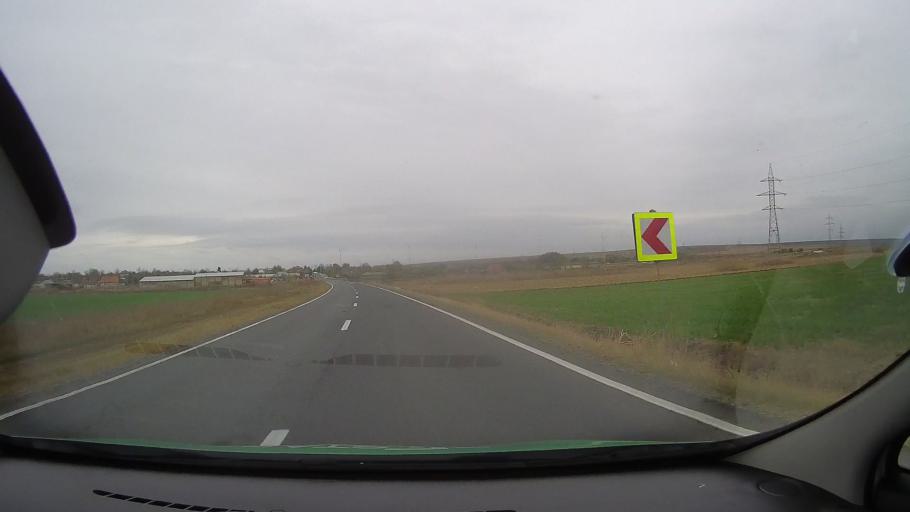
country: RO
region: Constanta
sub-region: Comuna Nicolae Balcescu
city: Dorobantu
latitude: 44.4140
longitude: 28.3181
